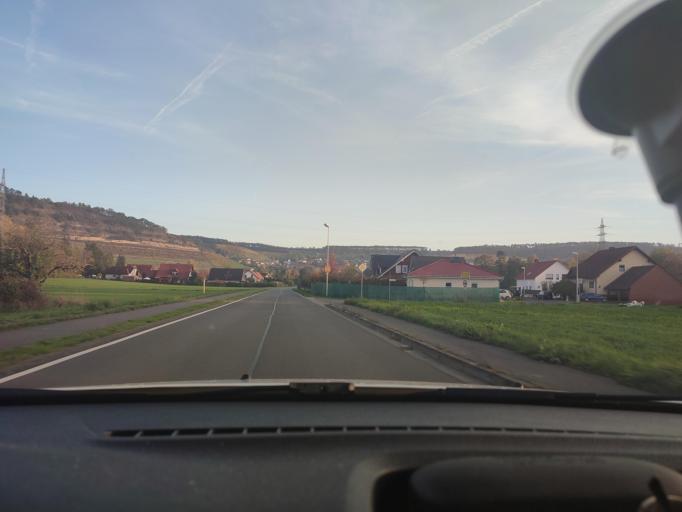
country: DE
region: Bavaria
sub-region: Regierungsbezirk Unterfranken
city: Marktheidenfeld
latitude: 49.8019
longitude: 9.6126
